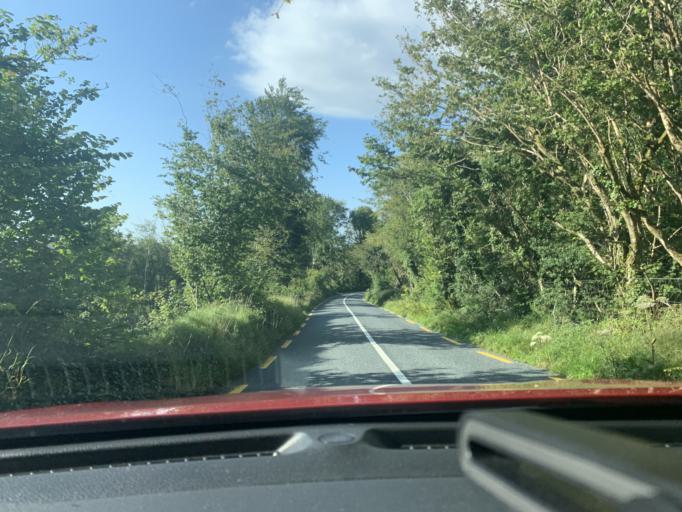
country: IE
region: Connaught
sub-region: Sligo
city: Strandhill
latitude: 54.1983
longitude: -8.5865
